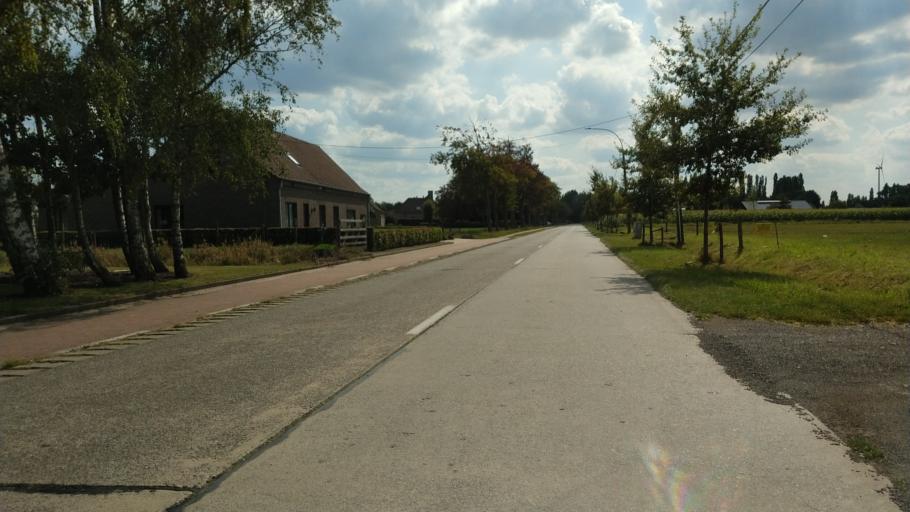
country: BE
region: Flanders
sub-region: Provincie Oost-Vlaanderen
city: Kaprijke
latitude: 51.2254
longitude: 3.6753
